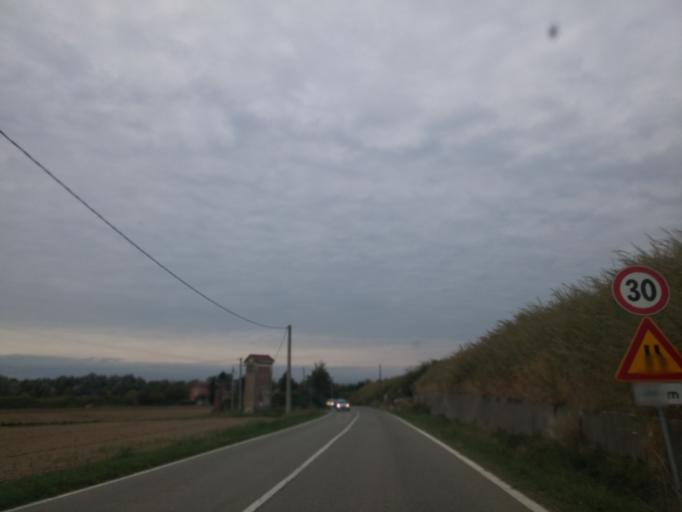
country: IT
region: Emilia-Romagna
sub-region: Provincia di Bologna
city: Longara
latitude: 44.5922
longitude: 11.3211
